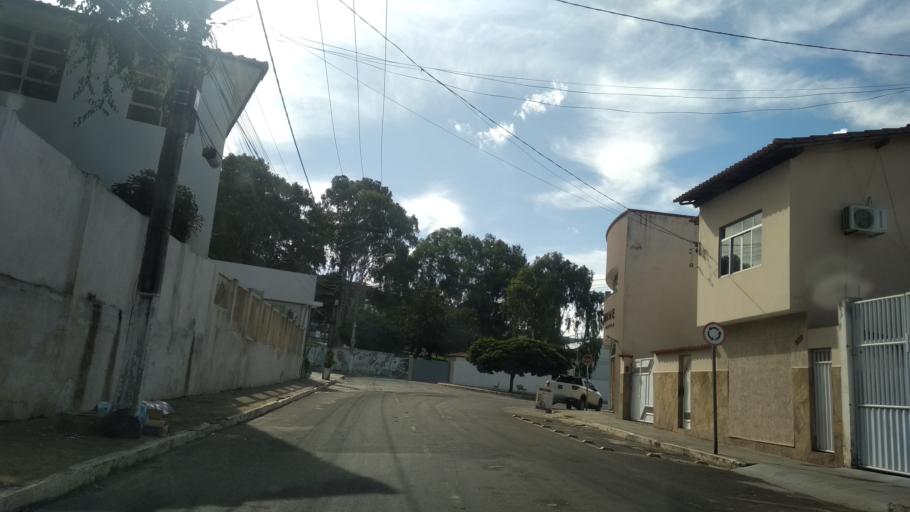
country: BR
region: Bahia
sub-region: Caetite
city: Caetite
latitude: -14.0688
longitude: -42.4920
